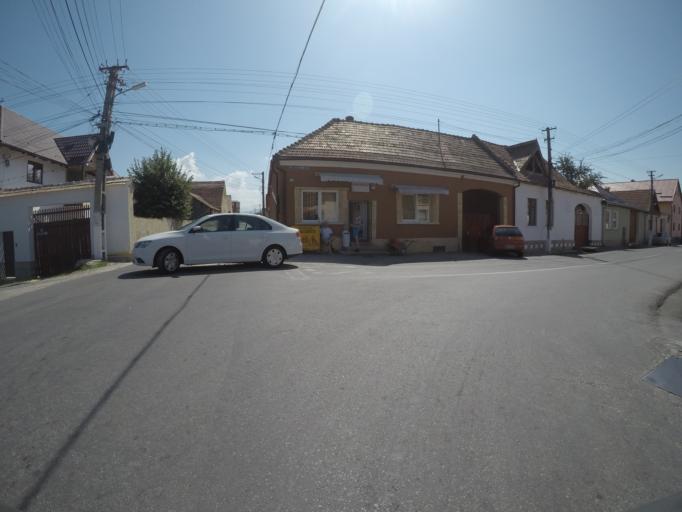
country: RO
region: Brasov
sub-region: Comuna Zarnesti
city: Tohanu Nou
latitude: 45.5524
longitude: 25.3833
